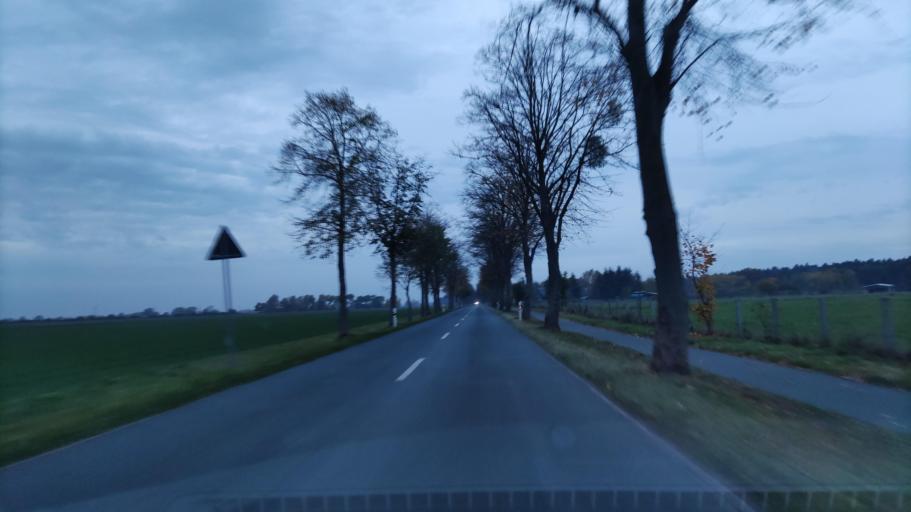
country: DE
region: Lower Saxony
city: Parsau
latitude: 52.5386
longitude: 10.8819
